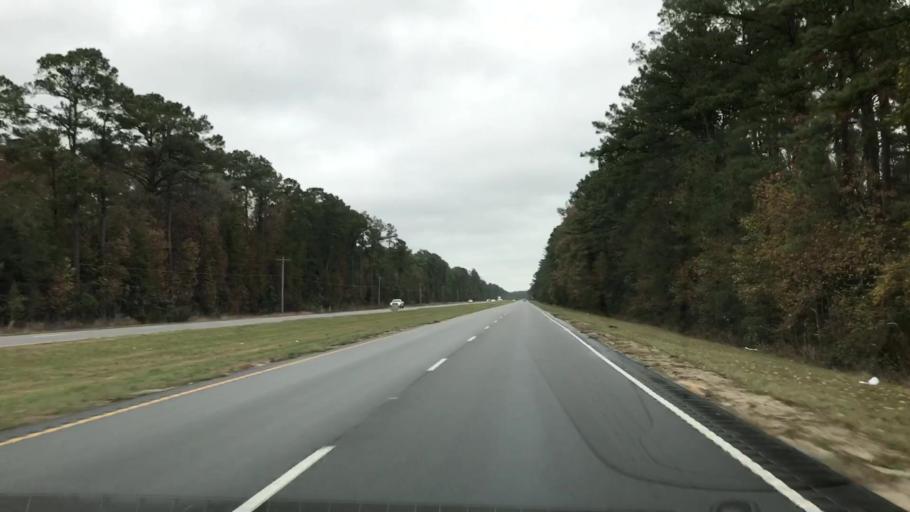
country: US
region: South Carolina
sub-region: Georgetown County
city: Georgetown
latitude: 33.2581
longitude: -79.3686
